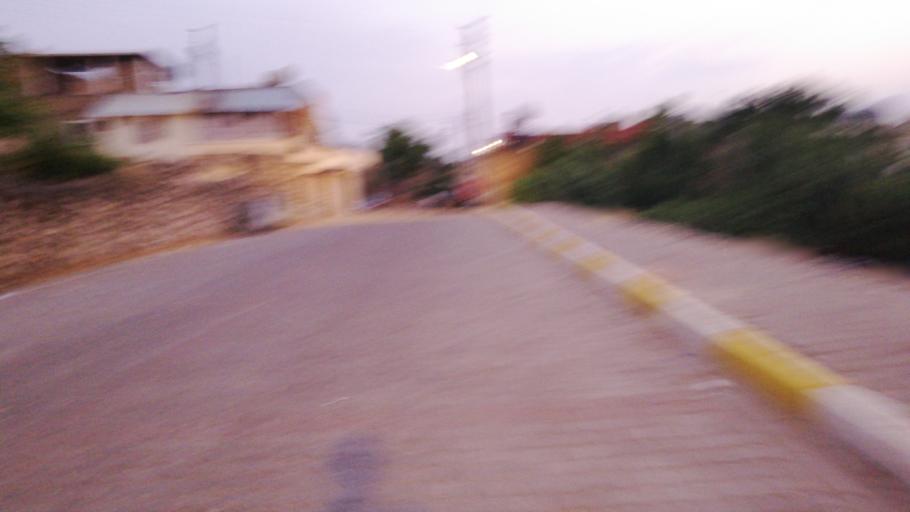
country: TR
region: Mardin
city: Kindirip
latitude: 37.4477
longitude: 41.2200
